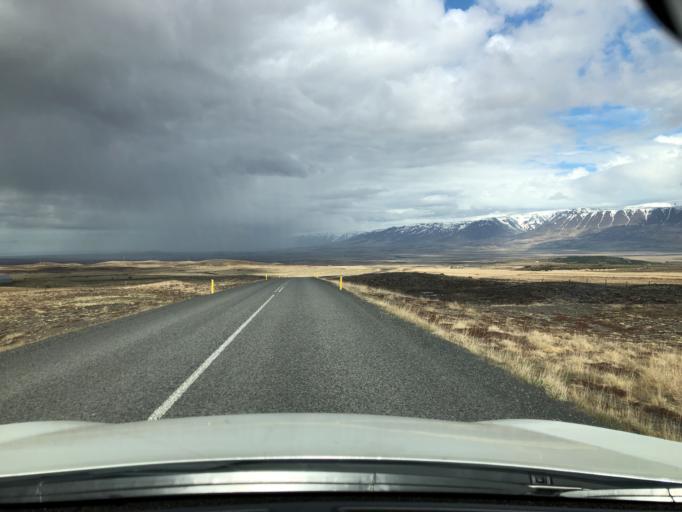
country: IS
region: Northwest
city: Saudarkrokur
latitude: 65.5326
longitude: -19.5127
